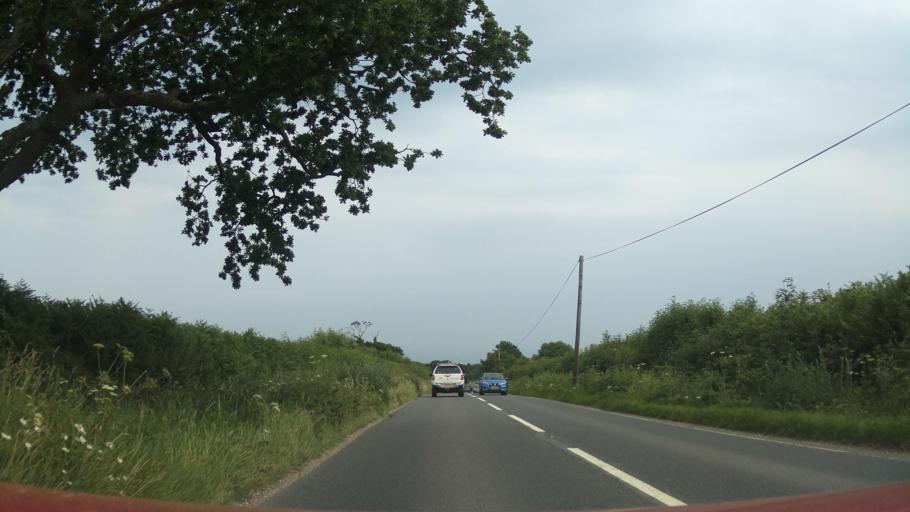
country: GB
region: England
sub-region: Devon
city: Colyton
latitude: 50.7147
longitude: -3.1469
